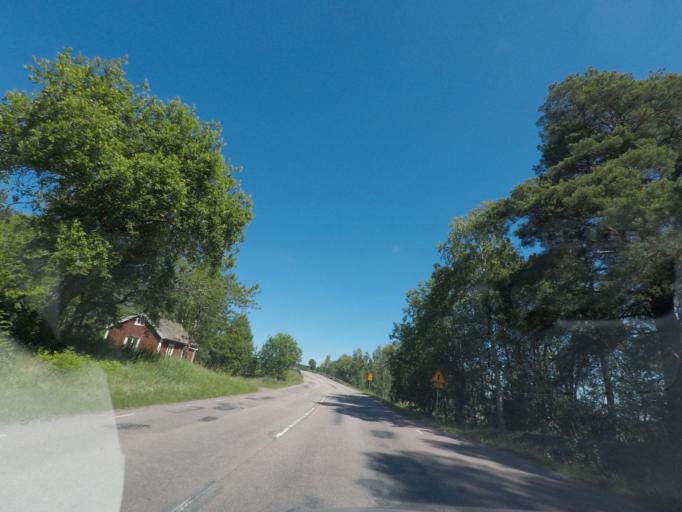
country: SE
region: Vaestmanland
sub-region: Vasteras
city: Tillberga
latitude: 59.6688
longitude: 16.7227
